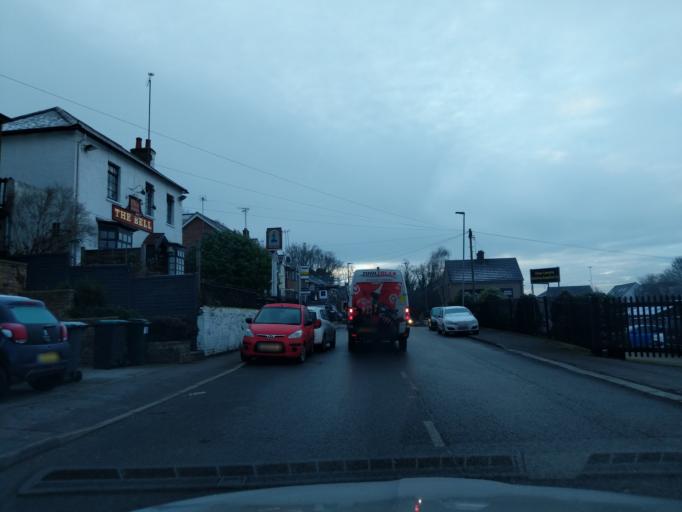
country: GB
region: England
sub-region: Hertfordshire
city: Kings Langley
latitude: 51.7152
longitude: -0.4418
